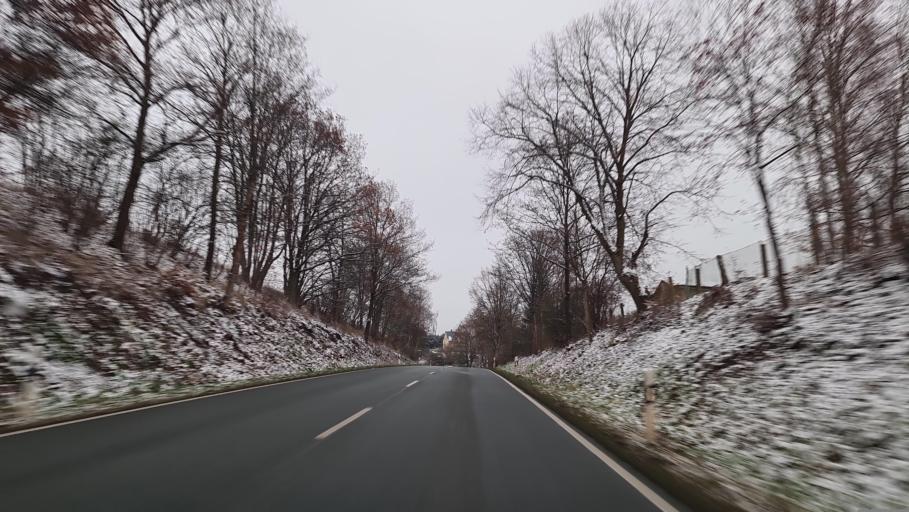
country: DE
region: Saxony
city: Markneukirchen
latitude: 50.3148
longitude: 12.3200
